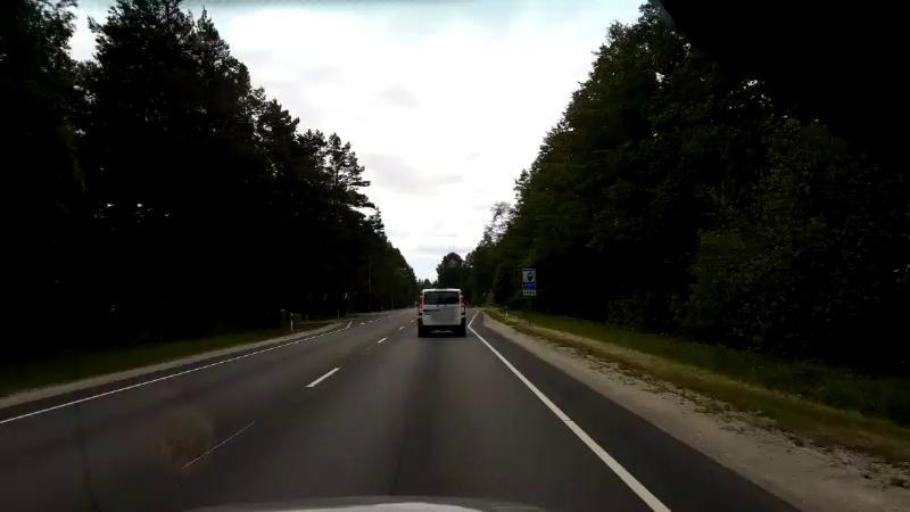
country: EE
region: Paernumaa
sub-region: Paernu linn
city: Parnu
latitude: 58.2160
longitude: 24.4870
